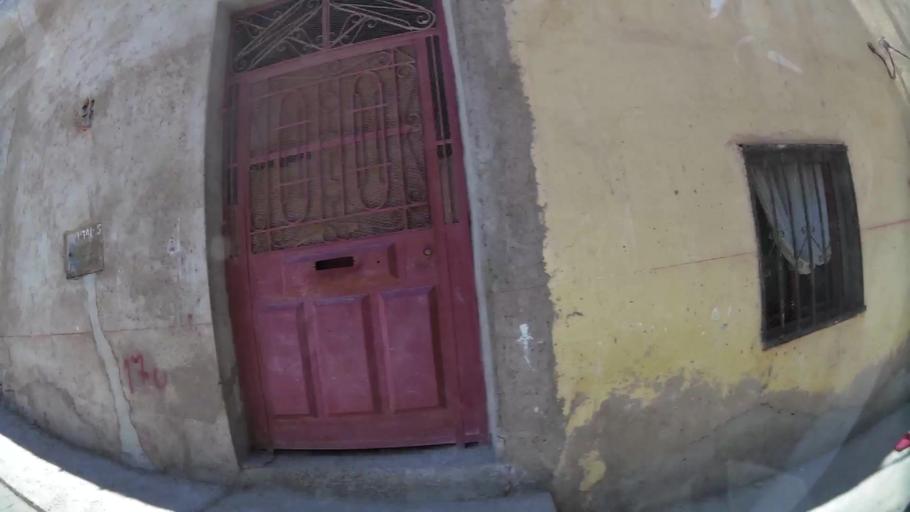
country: MA
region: Oriental
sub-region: Oujda-Angad
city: Oujda
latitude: 34.6779
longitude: -1.9539
